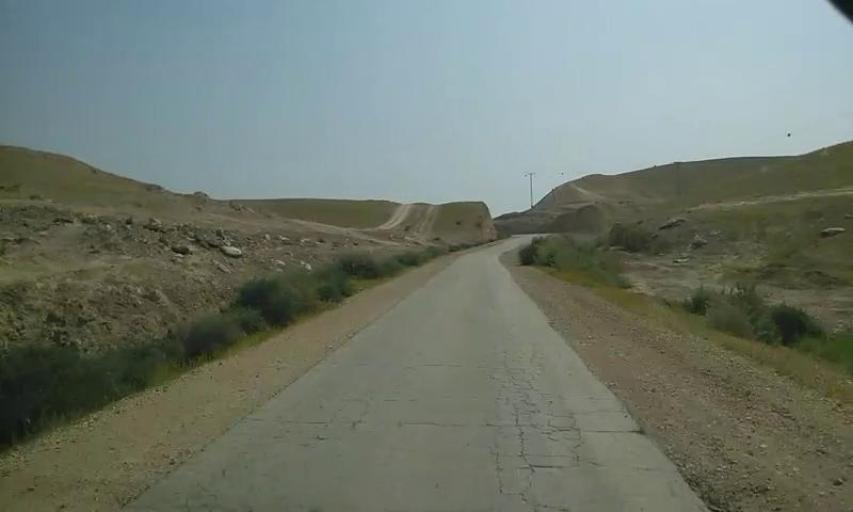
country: PS
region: West Bank
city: Jericho
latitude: 31.7931
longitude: 35.4274
